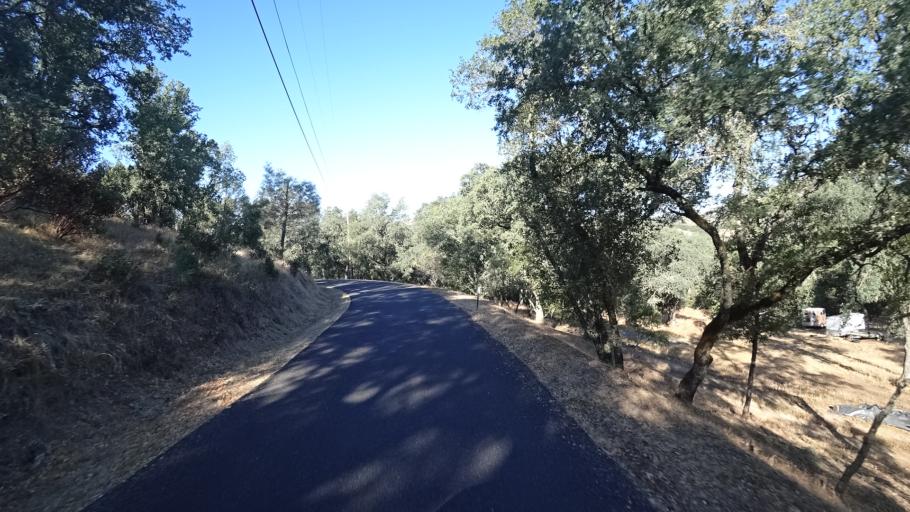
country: US
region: California
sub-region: Calaveras County
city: San Andreas
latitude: 38.2391
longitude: -120.7157
